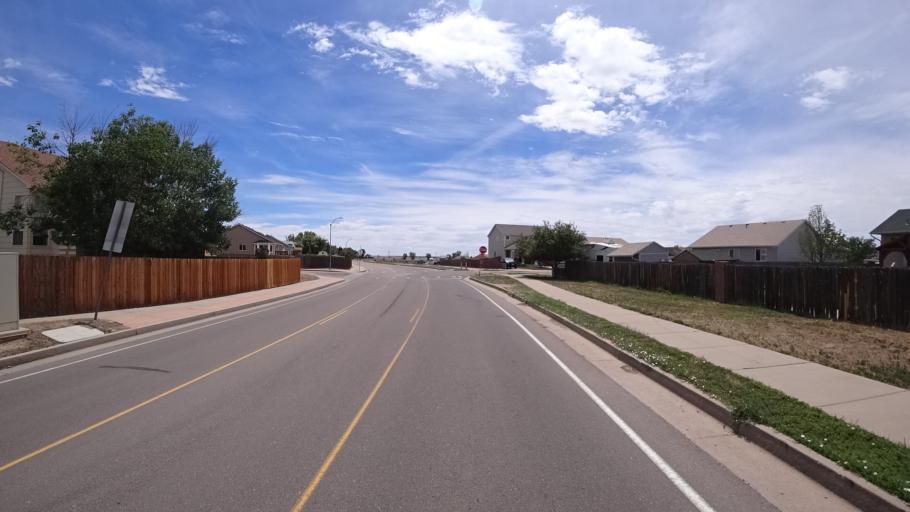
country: US
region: Colorado
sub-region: El Paso County
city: Fountain
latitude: 38.6683
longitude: -104.6826
